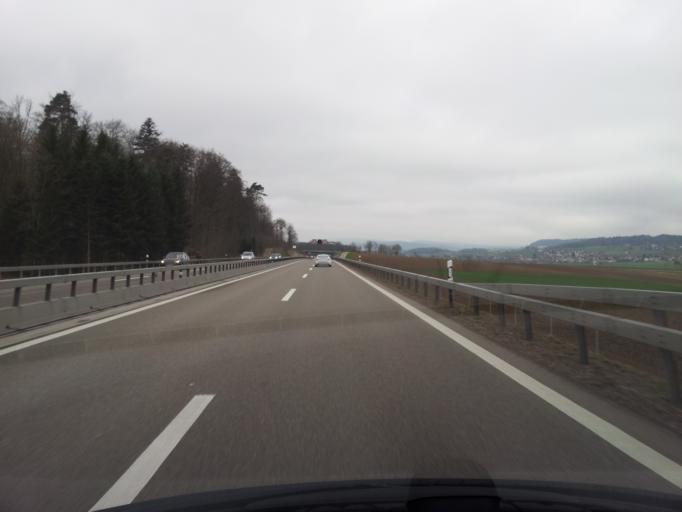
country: CH
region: Zurich
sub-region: Bezirk Andelfingen
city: Marthalen
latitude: 47.6321
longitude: 8.6680
